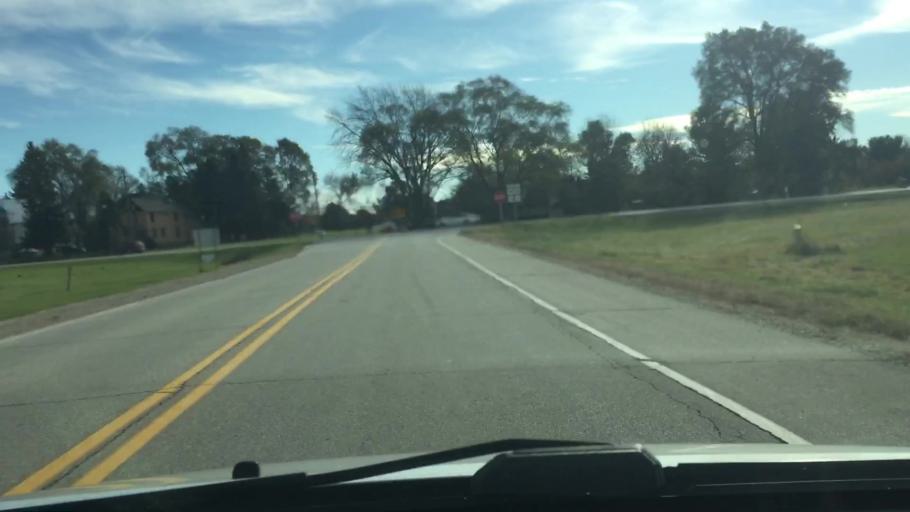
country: US
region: Wisconsin
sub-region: Waukesha County
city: North Prairie
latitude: 42.9443
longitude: -88.3785
